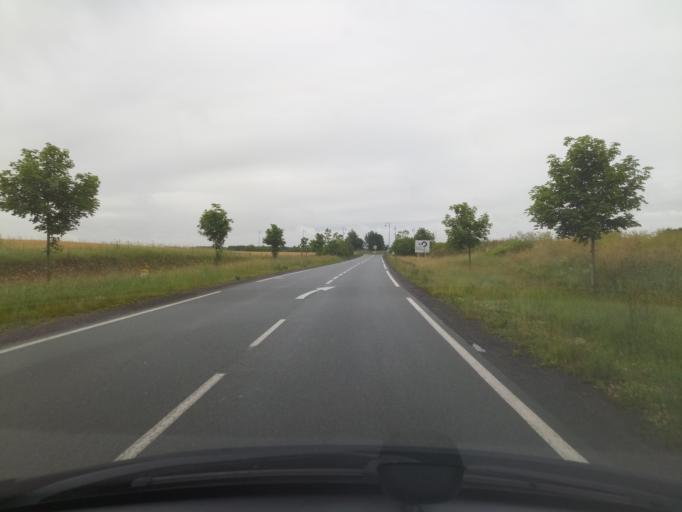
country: FR
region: Poitou-Charentes
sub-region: Departement de la Charente-Maritime
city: Courcon
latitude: 46.1850
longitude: -0.8546
